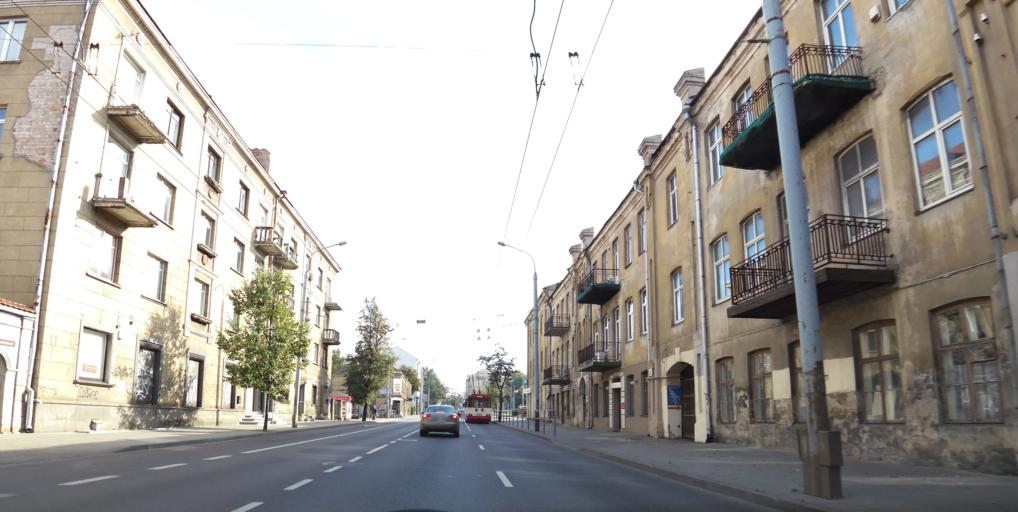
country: LT
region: Vilnius County
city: Naujamiestis
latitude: 54.6879
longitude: 25.2656
